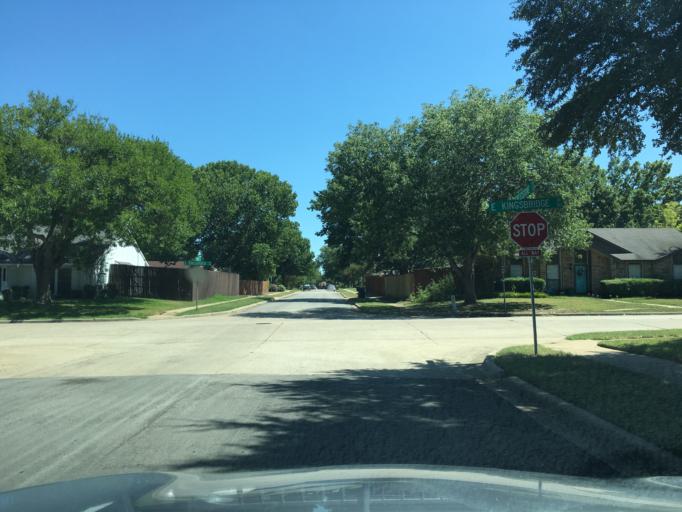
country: US
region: Texas
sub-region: Dallas County
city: Garland
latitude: 32.9519
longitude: -96.6282
